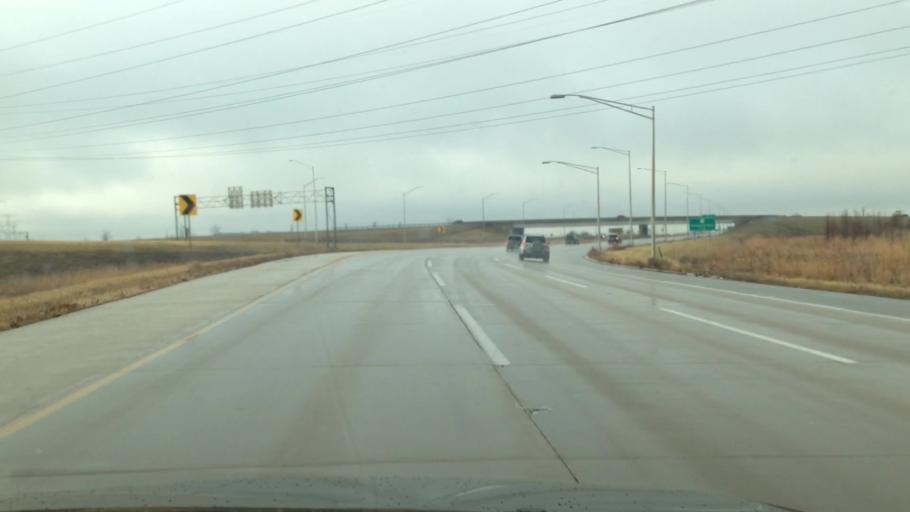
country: US
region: Illinois
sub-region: Will County
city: New Lenox
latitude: 41.5418
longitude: -87.9629
